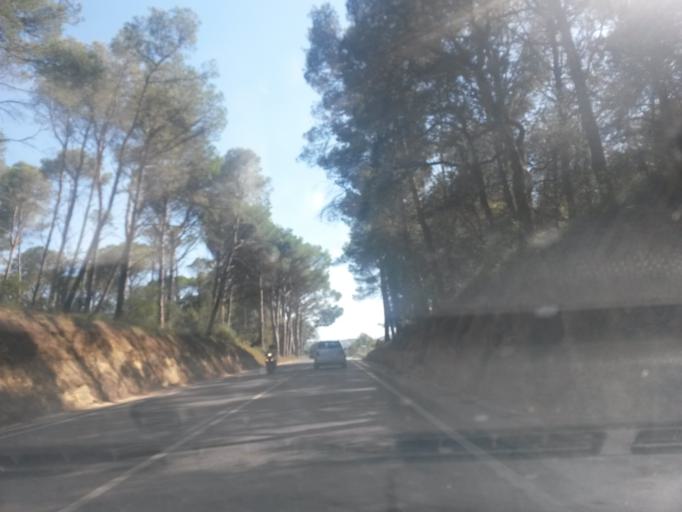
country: ES
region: Catalonia
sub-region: Provincia de Girona
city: Regencos
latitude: 41.9397
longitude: 3.1619
